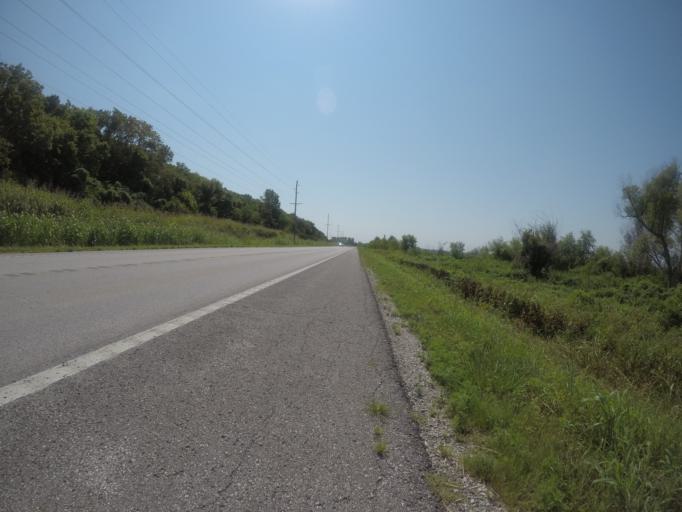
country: US
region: Kansas
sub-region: Atchison County
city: Atchison
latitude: 39.5382
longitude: -95.0405
